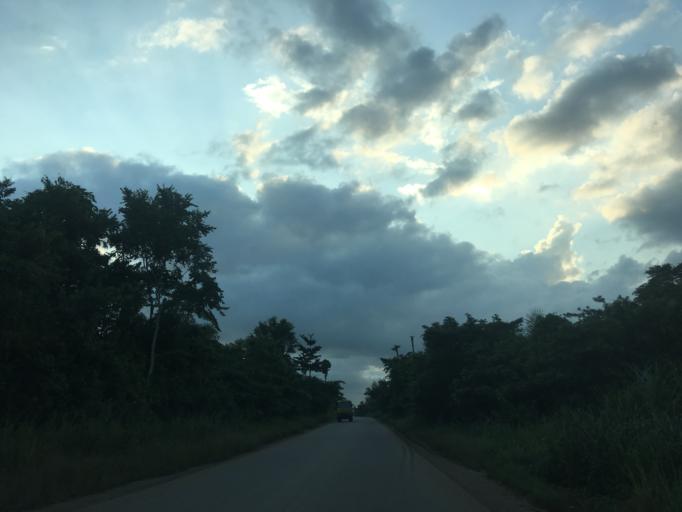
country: GH
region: Western
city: Bibiani
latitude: 6.7146
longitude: -2.4595
